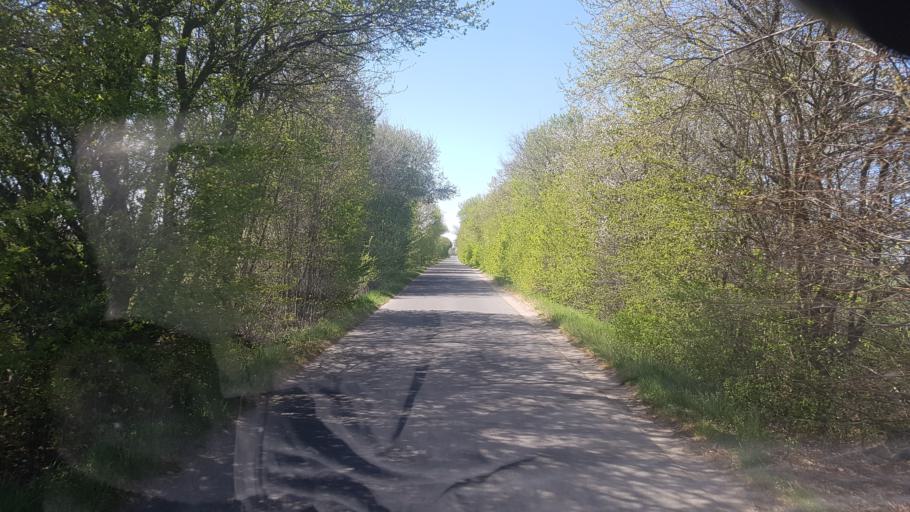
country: DE
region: Brandenburg
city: Sonnewalde
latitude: 51.7191
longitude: 13.6418
